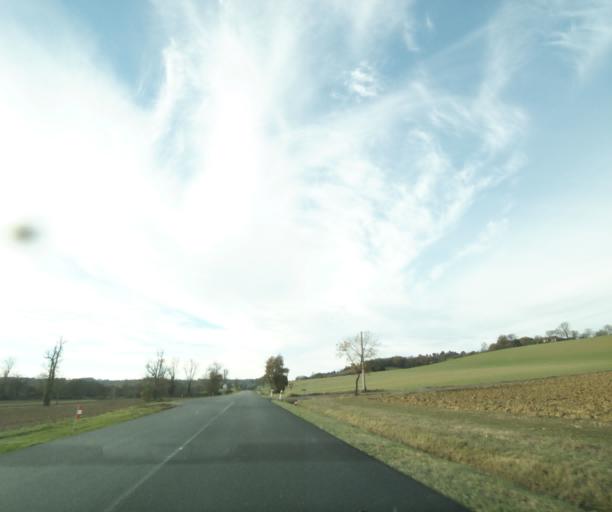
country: FR
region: Midi-Pyrenees
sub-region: Departement du Gers
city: Jegun
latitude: 43.6918
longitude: 0.4722
